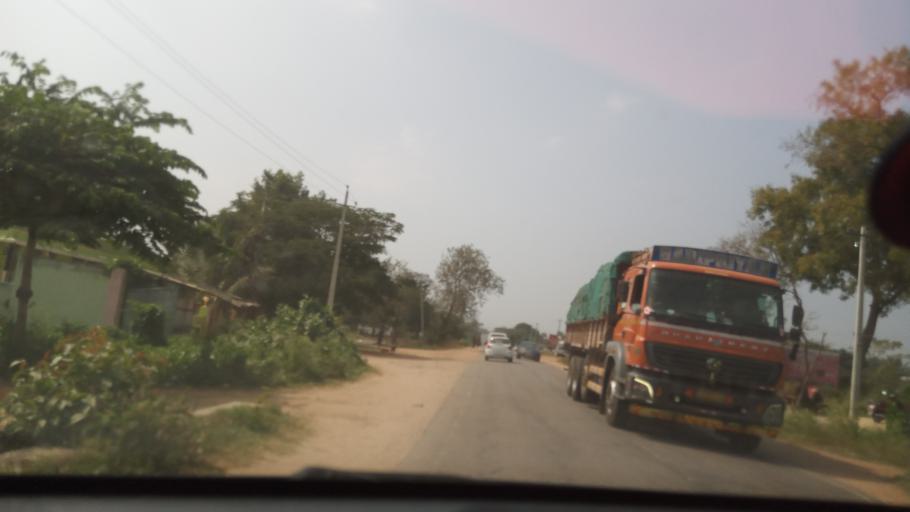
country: IN
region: Karnataka
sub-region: Chamrajnagar
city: Chamrajnagar
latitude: 11.9940
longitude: 76.8584
